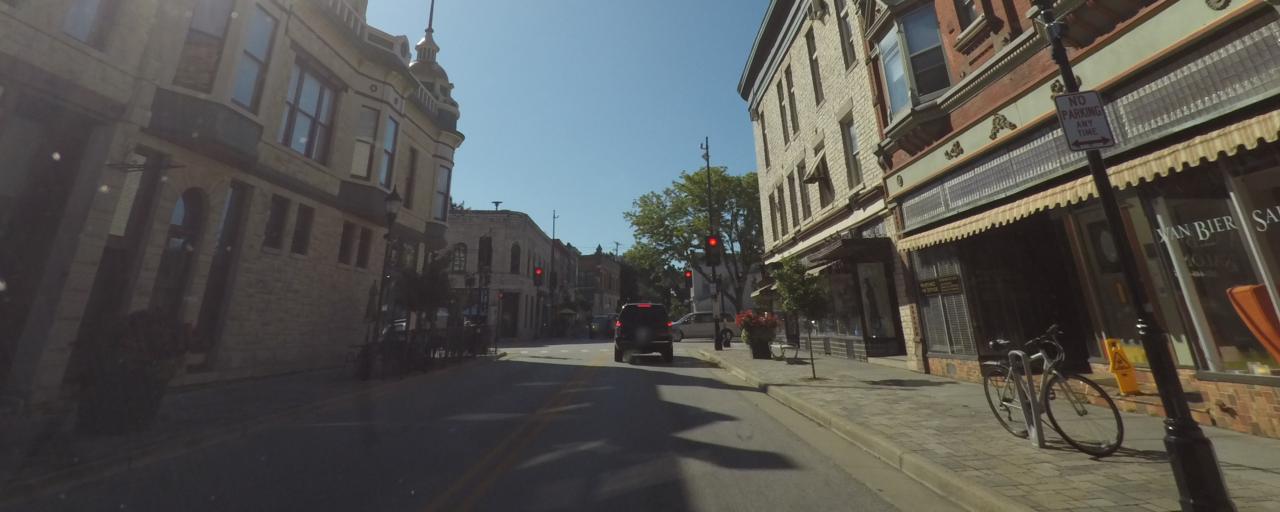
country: US
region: Wisconsin
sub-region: Waukesha County
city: Waukesha
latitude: 43.0116
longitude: -88.2329
